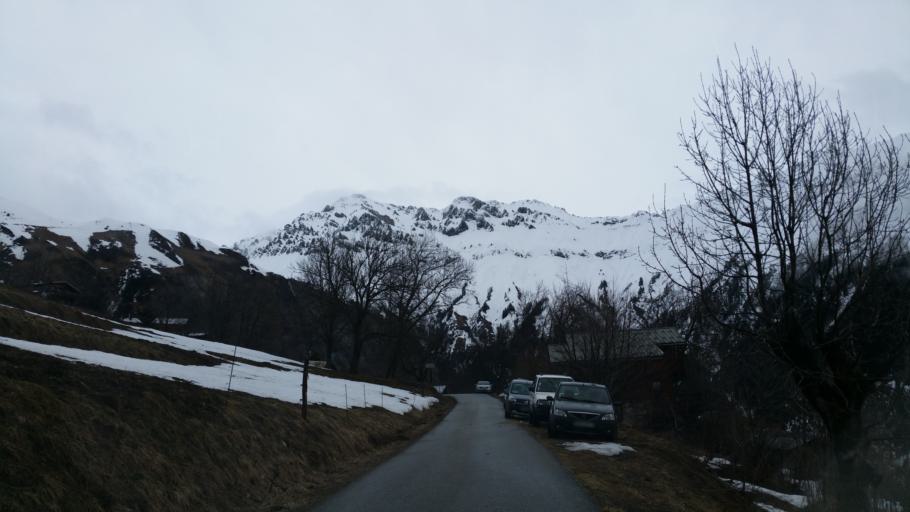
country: FR
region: Rhone-Alpes
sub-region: Departement de la Savoie
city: Villargondran
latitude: 45.2832
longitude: 6.4058
